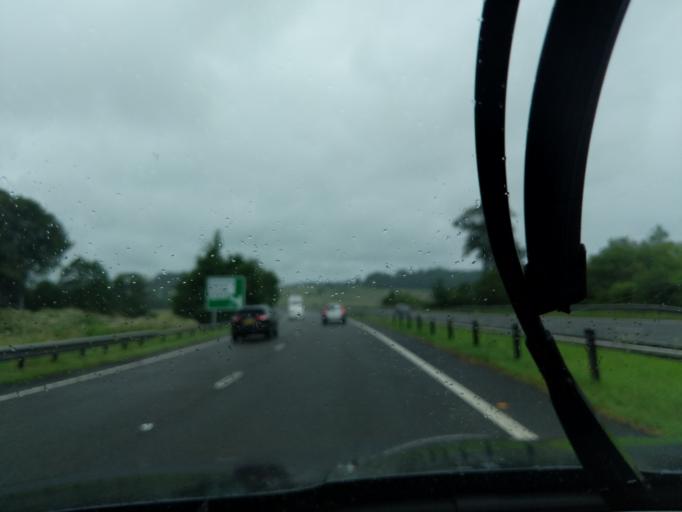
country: GB
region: England
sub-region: Northumberland
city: Alnwick
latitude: 55.4112
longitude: -1.6768
